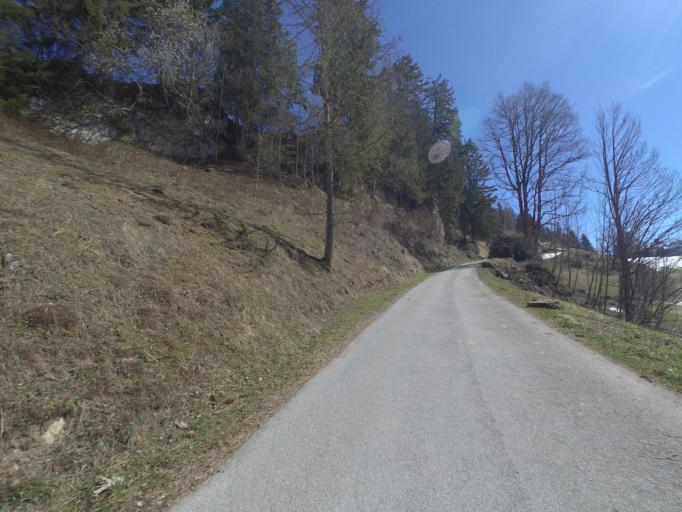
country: AT
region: Salzburg
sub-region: Politischer Bezirk Sankt Johann im Pongau
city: Sankt Veit im Pongau
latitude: 47.3400
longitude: 13.1556
